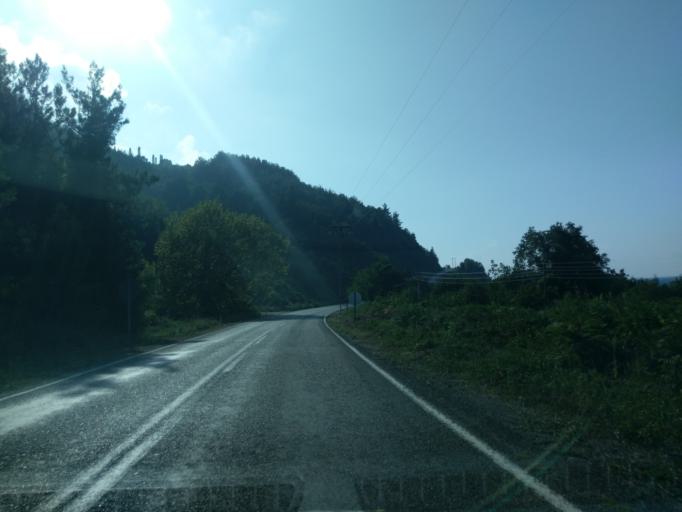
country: TR
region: Sinop
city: Ayancik
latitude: 41.9405
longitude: 34.6478
